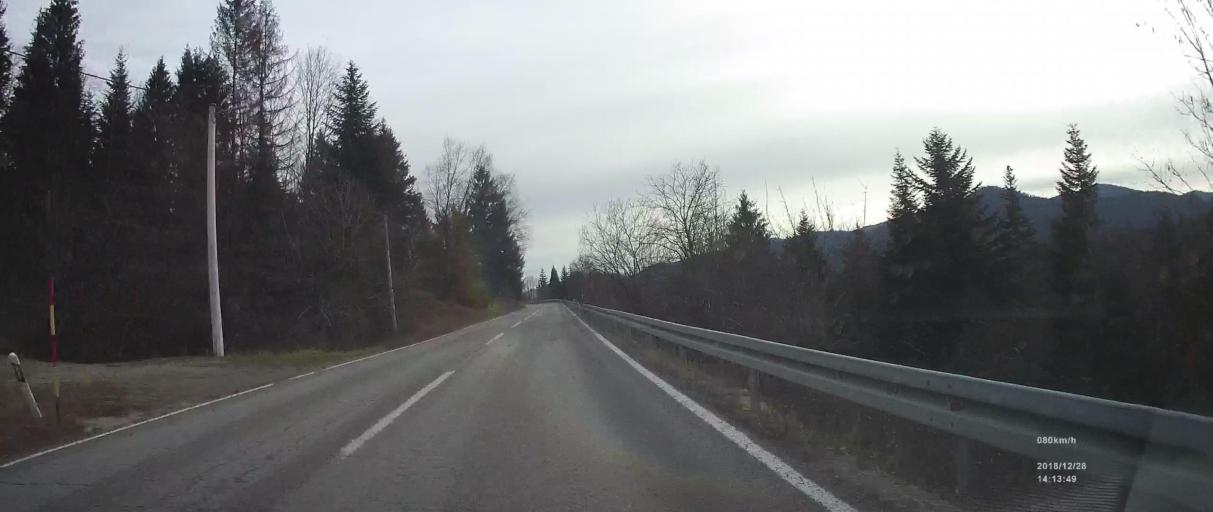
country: HR
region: Primorsko-Goranska
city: Vrbovsko
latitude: 45.4362
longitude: 15.0120
